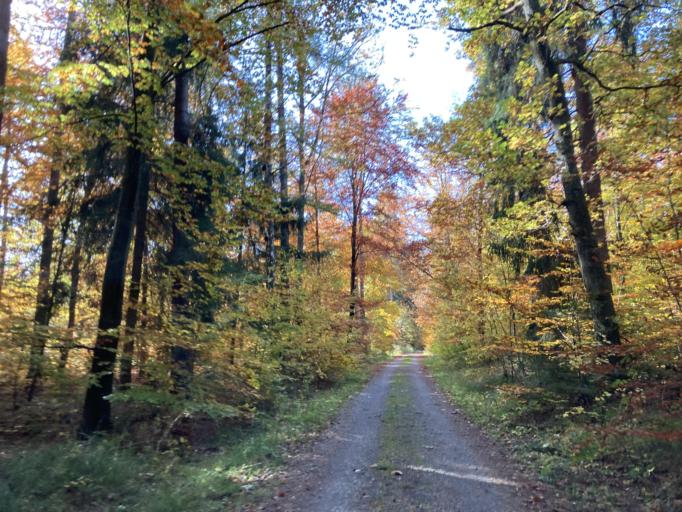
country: DE
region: Baden-Wuerttemberg
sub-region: Tuebingen Region
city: Rottenburg
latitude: 48.4614
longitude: 8.9794
